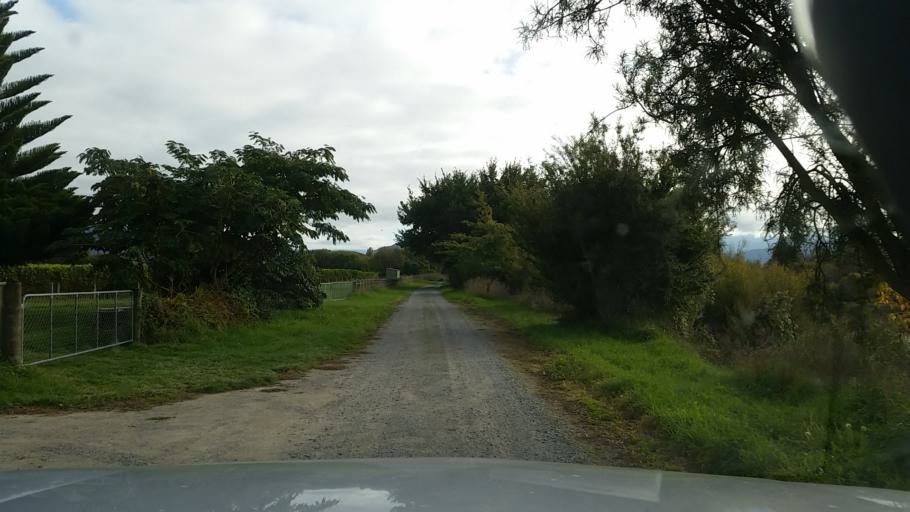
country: NZ
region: Marlborough
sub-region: Marlborough District
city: Blenheim
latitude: -41.4739
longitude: 173.9805
